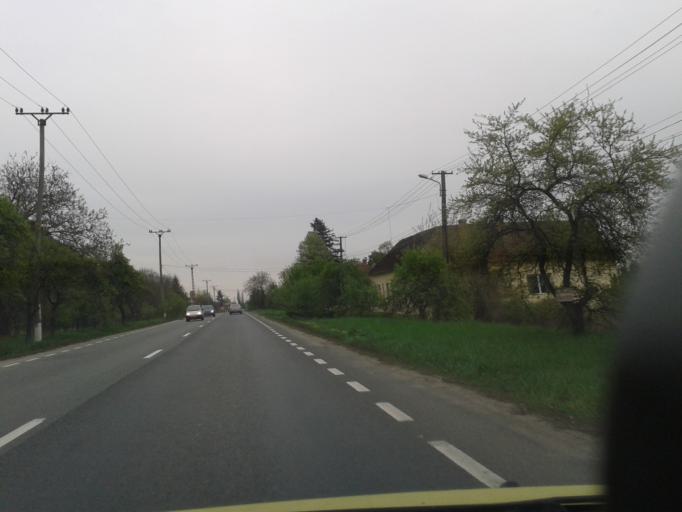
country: RO
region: Arad
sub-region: Comuna Paulis
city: Paulis
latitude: 46.1087
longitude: 21.6060
